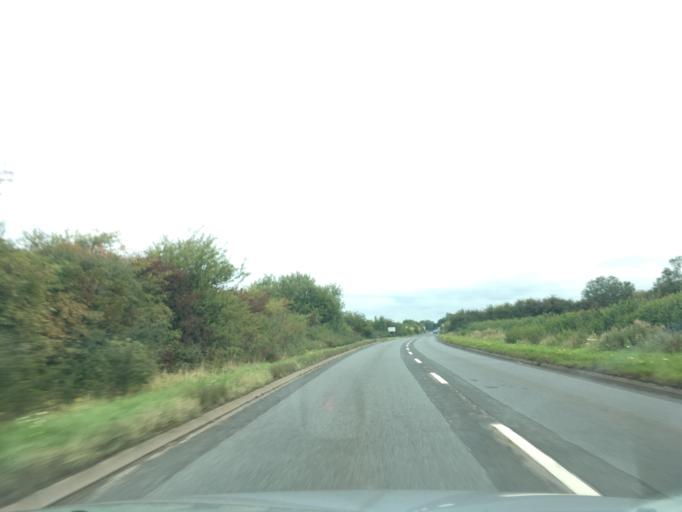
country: GB
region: England
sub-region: Oxfordshire
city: Banbury
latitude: 52.0784
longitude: -1.3133
